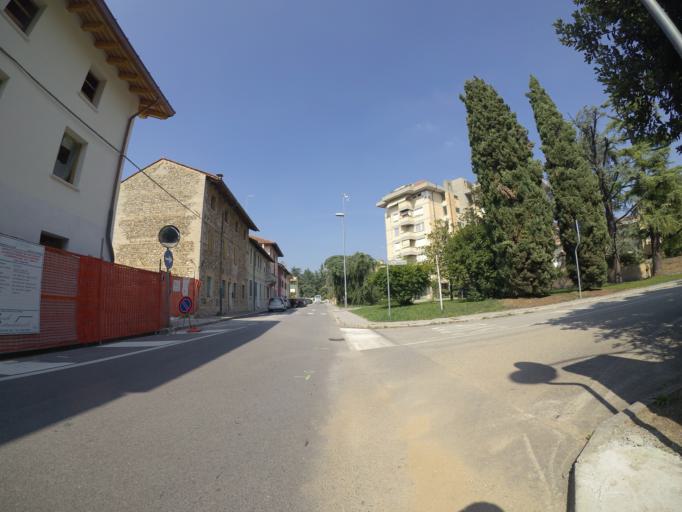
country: IT
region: Friuli Venezia Giulia
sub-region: Provincia di Udine
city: Codroipo
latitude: 45.9619
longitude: 12.9826
